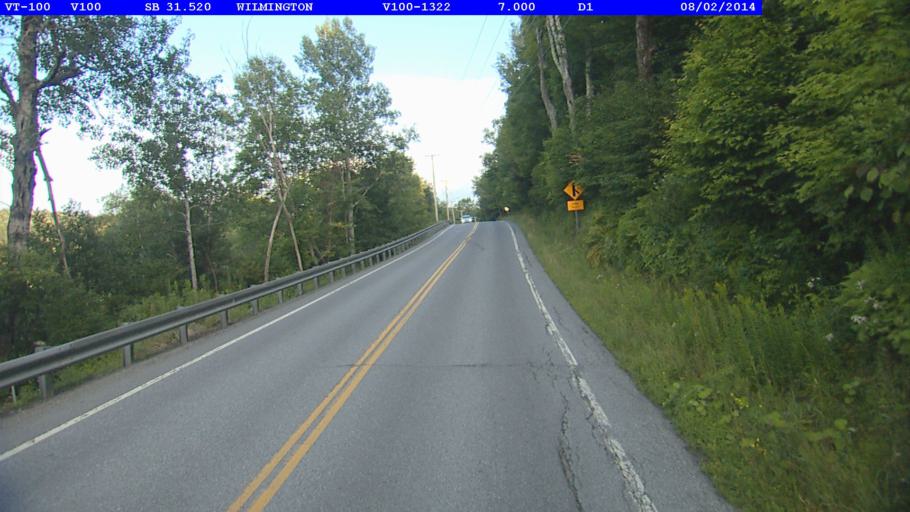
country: US
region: Vermont
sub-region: Windham County
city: Dover
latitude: 42.9216
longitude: -72.8424
